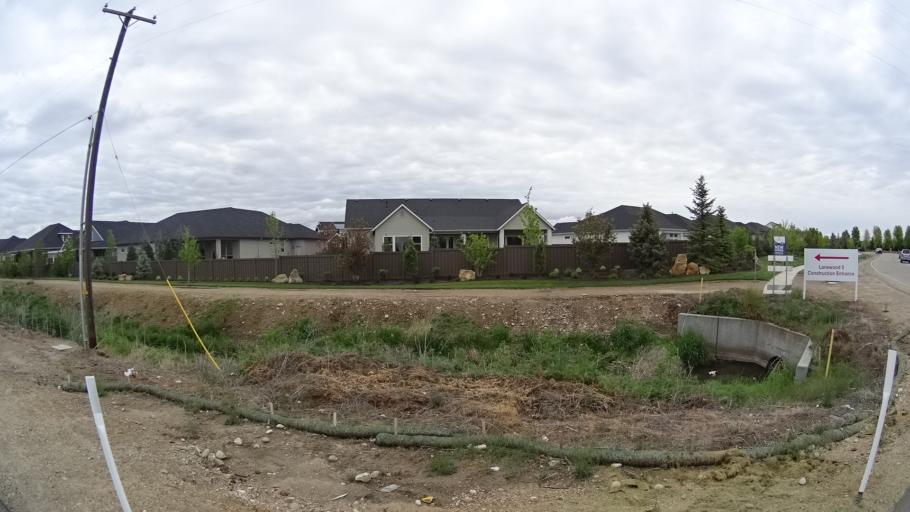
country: US
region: Idaho
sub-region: Ada County
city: Eagle
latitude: 43.7076
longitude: -116.4236
